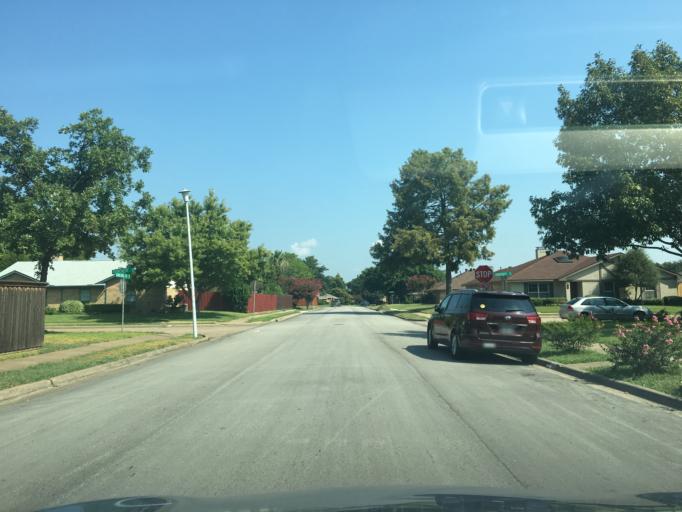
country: US
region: Texas
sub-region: Dallas County
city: Garland
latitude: 32.9461
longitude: -96.6327
